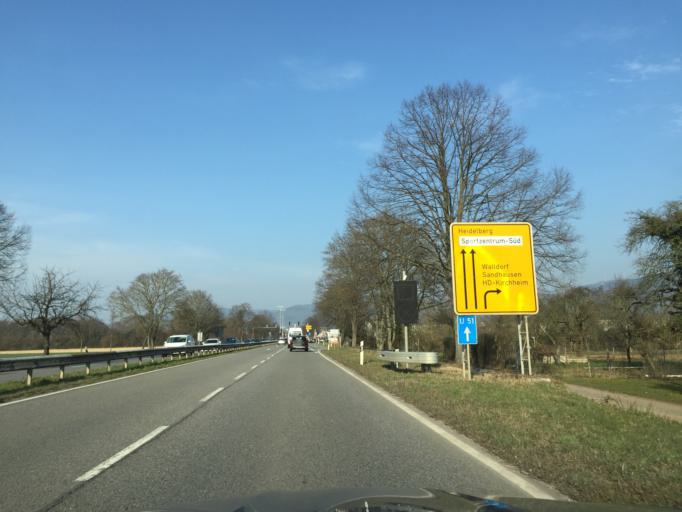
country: DE
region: Baden-Wuerttemberg
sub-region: Karlsruhe Region
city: Eppelheim
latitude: 49.3821
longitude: 8.6537
